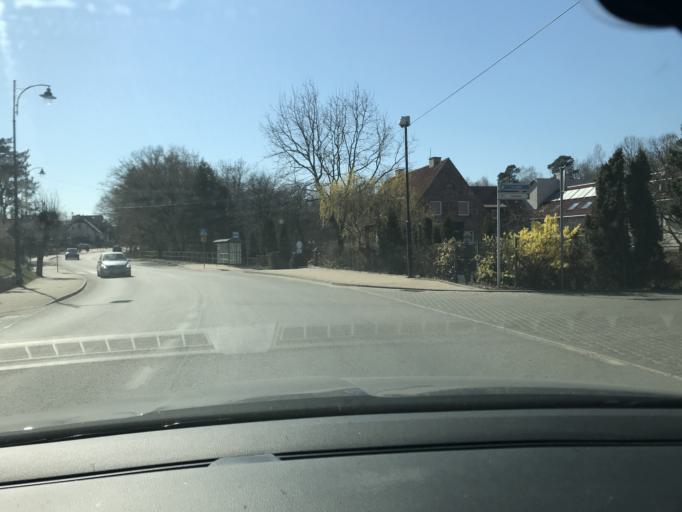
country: PL
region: Pomeranian Voivodeship
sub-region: Powiat nowodworski
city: Krynica Morska
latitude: 54.3768
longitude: 19.4323
